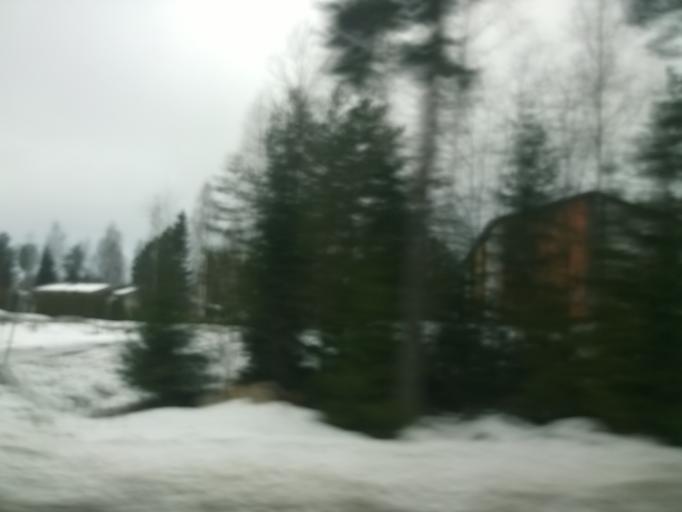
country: FI
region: Pirkanmaa
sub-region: Tampere
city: Lempaeaelae
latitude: 61.3931
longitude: 23.7764
